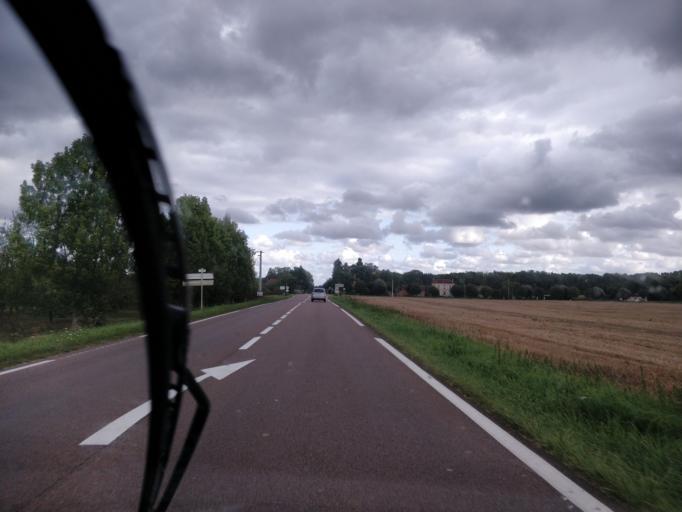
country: FR
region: Champagne-Ardenne
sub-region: Departement de l'Aube
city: Lusigny-sur-Barse
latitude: 48.2577
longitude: 4.2532
